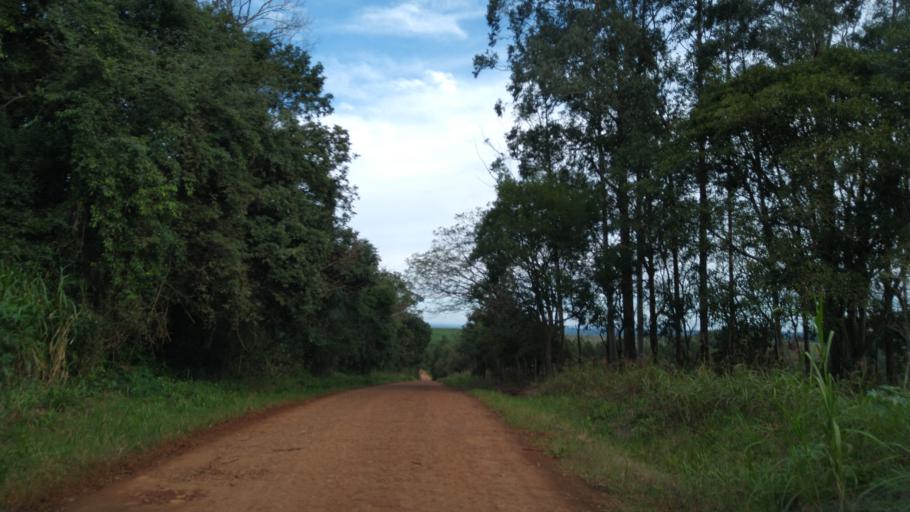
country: AR
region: Misiones
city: Capiovi
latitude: -26.9335
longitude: -55.0967
